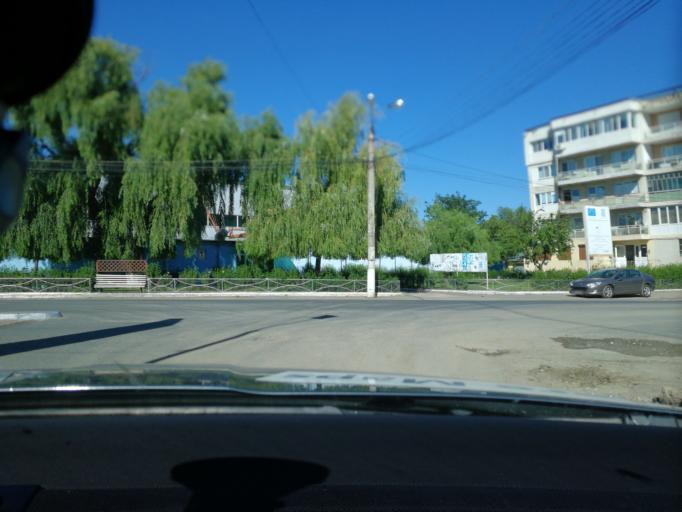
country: RO
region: Tulcea
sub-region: Oras Macin
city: Macin
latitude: 45.2470
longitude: 28.1276
